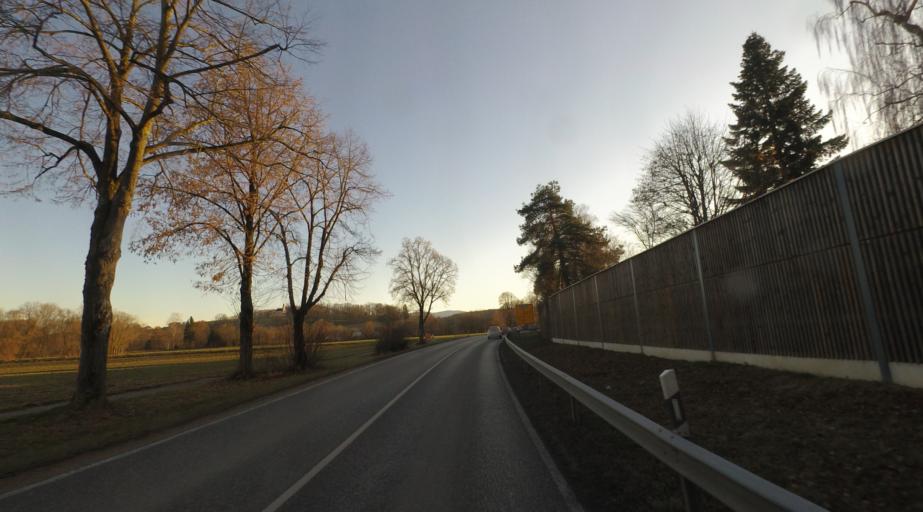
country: DE
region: Bavaria
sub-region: Upper Bavaria
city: Waging am See
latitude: 47.9373
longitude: 12.7442
